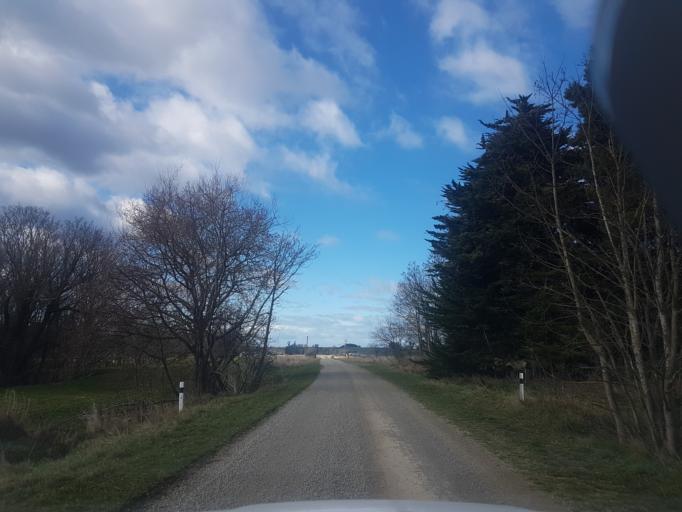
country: NZ
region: Canterbury
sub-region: Timaru District
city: Pleasant Point
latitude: -44.1885
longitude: 171.1751
